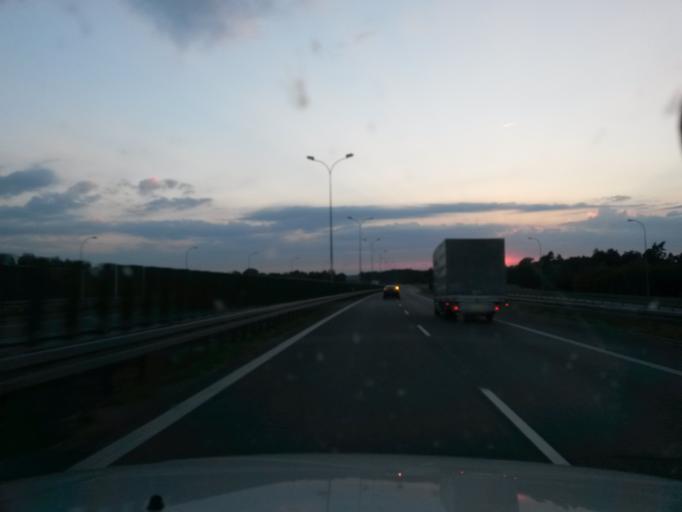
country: PL
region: Lower Silesian Voivodeship
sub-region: Powiat olesnicki
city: Olesnica
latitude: 51.2279
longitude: 17.4366
